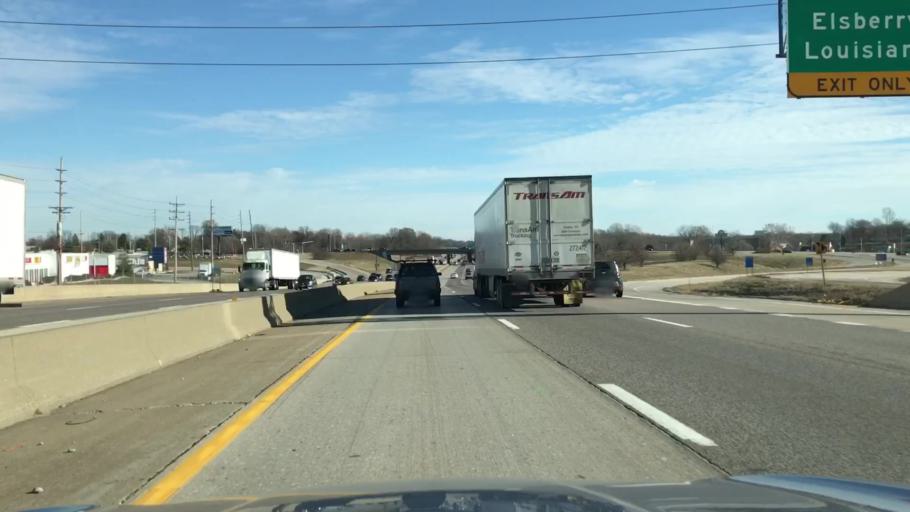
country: US
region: Missouri
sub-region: Saint Charles County
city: Saint Peters
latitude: 38.8025
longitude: -90.6607
